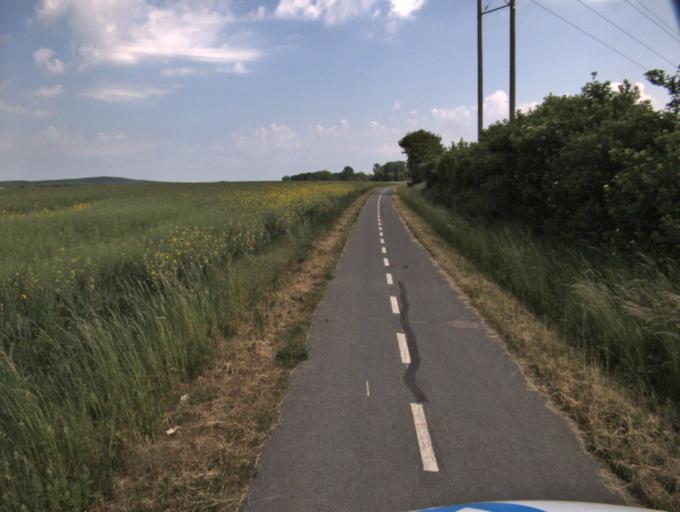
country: SE
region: Skane
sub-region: Kristianstads Kommun
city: Kristianstad
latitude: 56.0690
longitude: 14.1954
